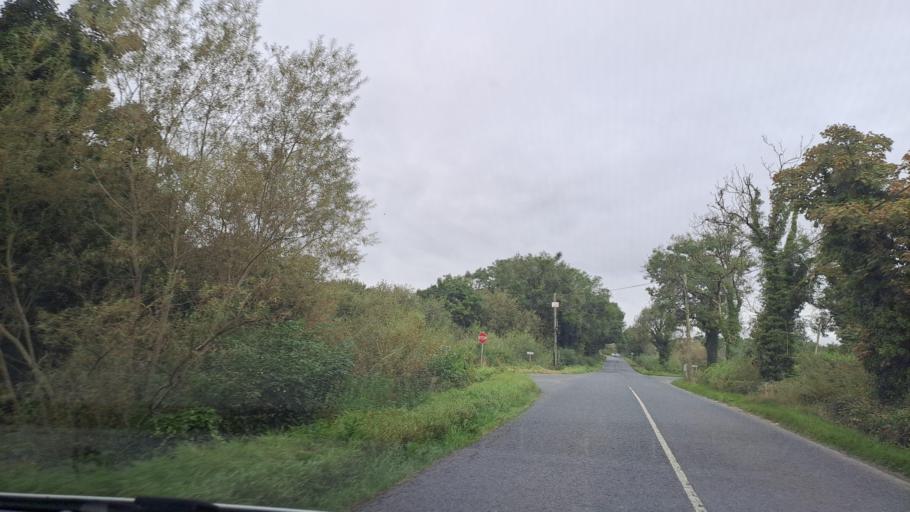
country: IE
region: Ulster
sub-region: An Cabhan
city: Kingscourt
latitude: 53.8828
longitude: -6.7354
